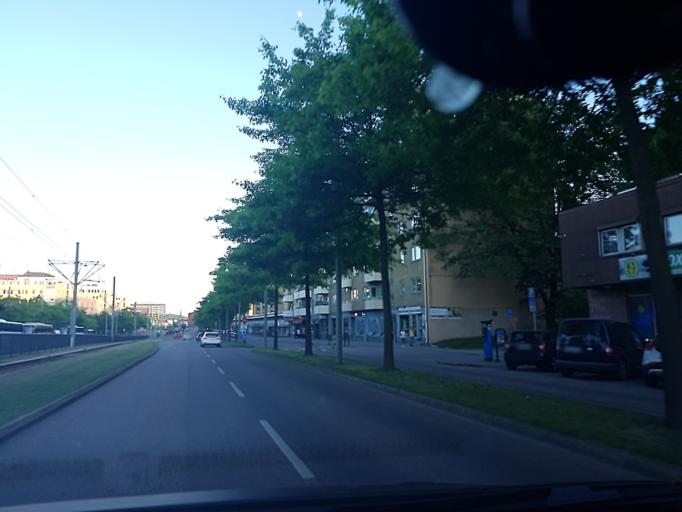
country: SE
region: Vaestra Goetaland
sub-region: Goteborg
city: Goeteborg
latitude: 57.6909
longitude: 11.9929
